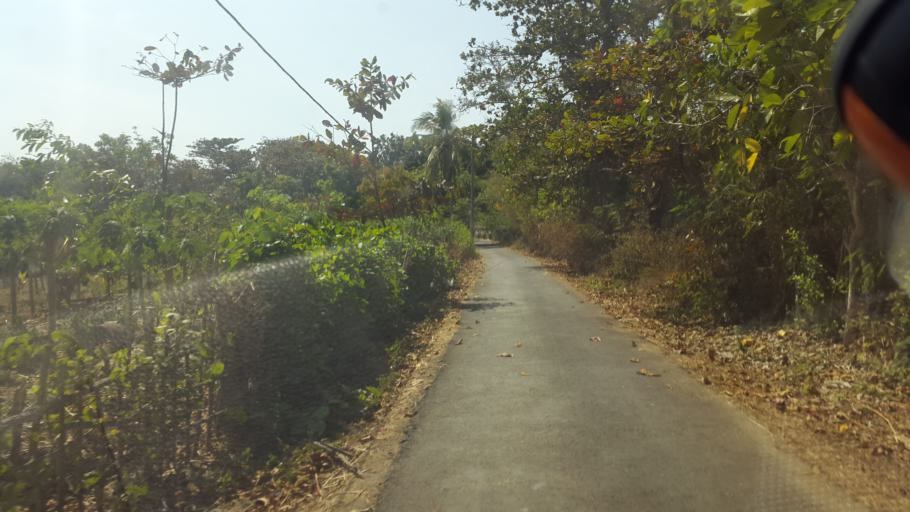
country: ID
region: West Java
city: Gunungbatu
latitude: -7.3394
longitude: 106.4010
